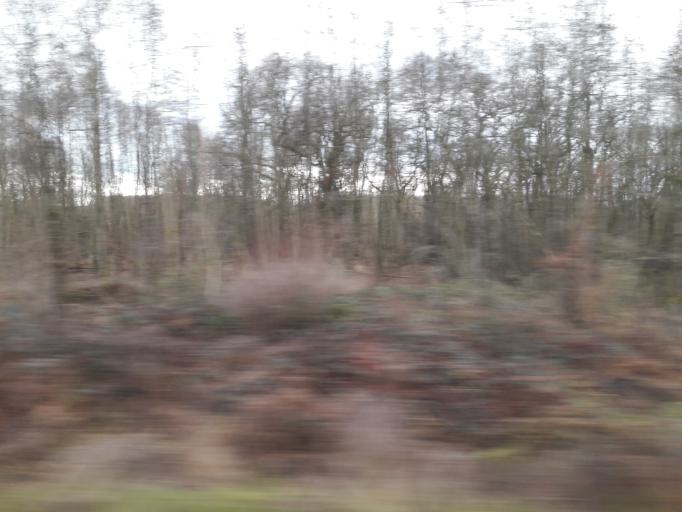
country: FR
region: Franche-Comte
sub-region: Territoire de Belfort
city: Joncherey
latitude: 47.5327
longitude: 6.9938
